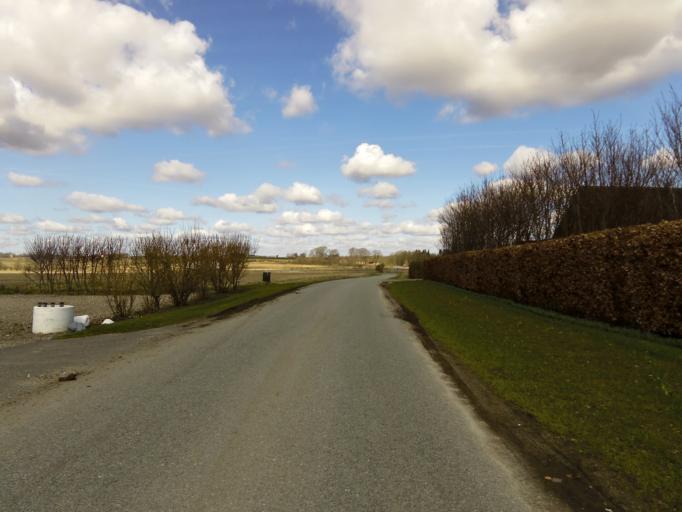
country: DK
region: South Denmark
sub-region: Tonder Kommune
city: Toftlund
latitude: 55.1672
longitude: 9.0524
